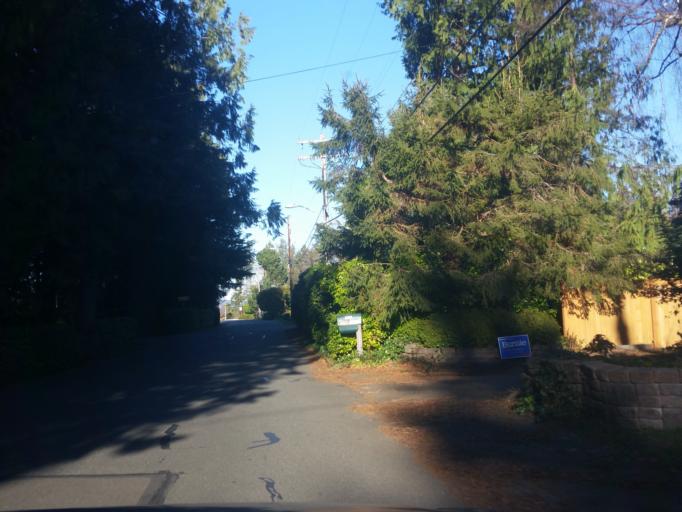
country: US
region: Washington
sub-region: Snohomish County
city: Edmonds
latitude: 47.8228
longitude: -122.3670
